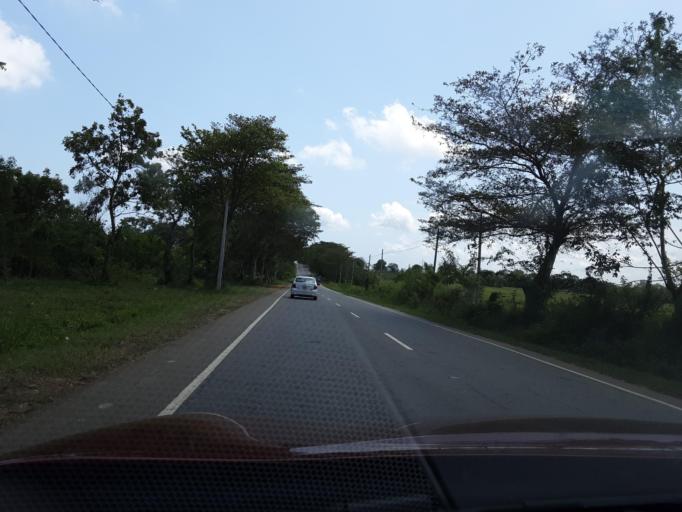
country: LK
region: Southern
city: Tangalla
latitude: 6.2311
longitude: 81.2254
